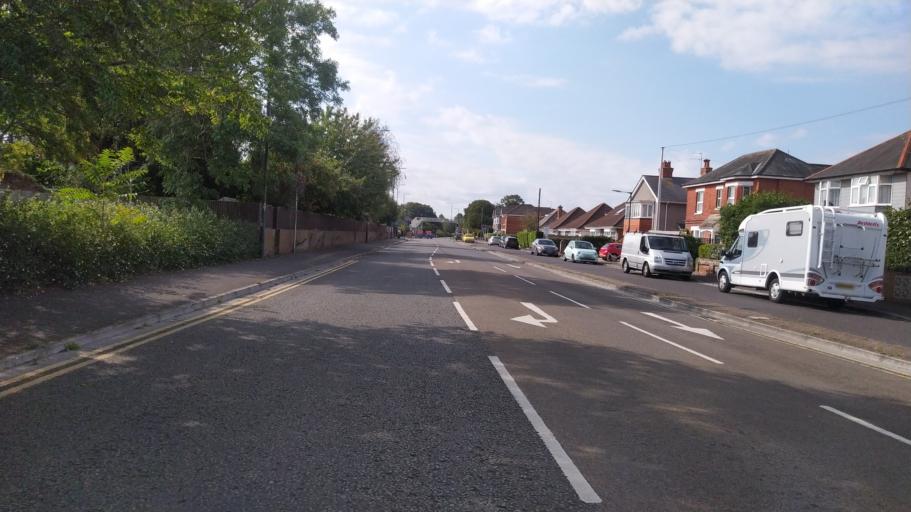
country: GB
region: England
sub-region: Bournemouth
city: Bournemouth
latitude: 50.7499
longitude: -1.8867
